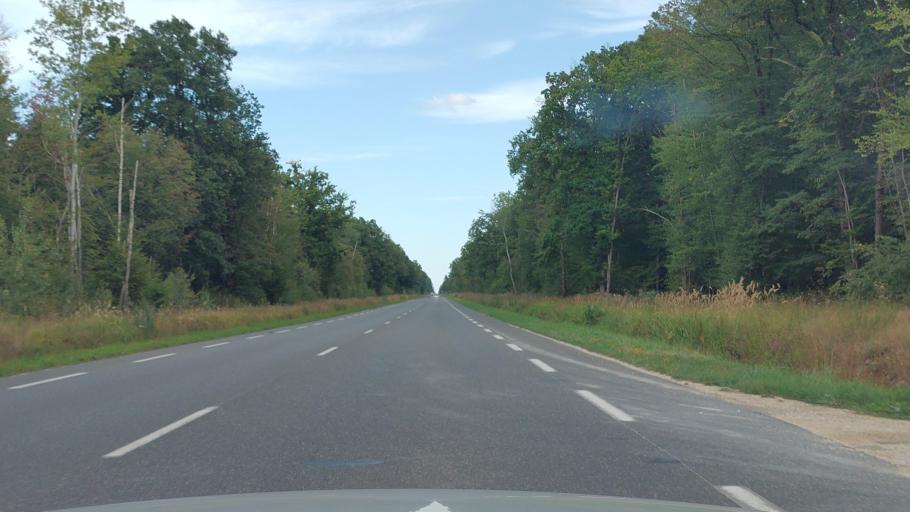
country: FR
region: Ile-de-France
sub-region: Departement de Seine-et-Marne
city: Le Chatelet-en-Brie
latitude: 48.5431
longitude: 2.8208
